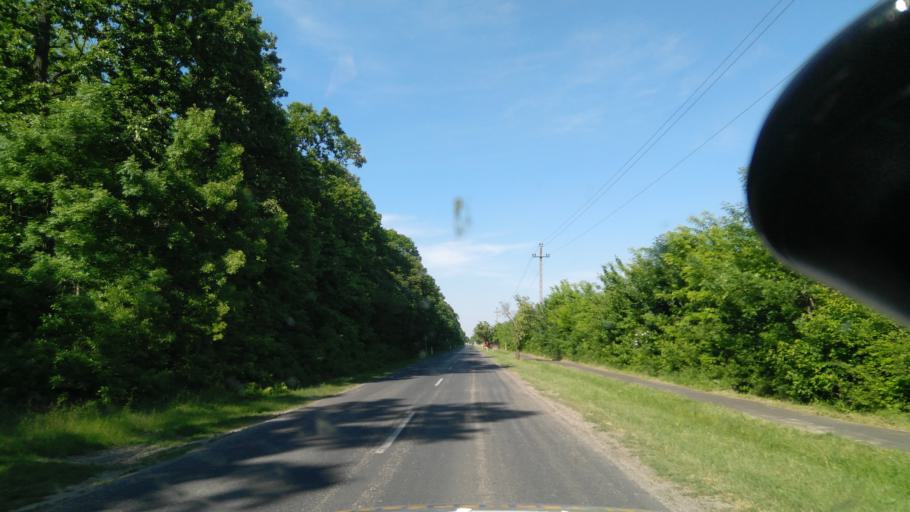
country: HU
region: Bekes
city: Sarkad
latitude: 46.7116
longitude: 21.3245
